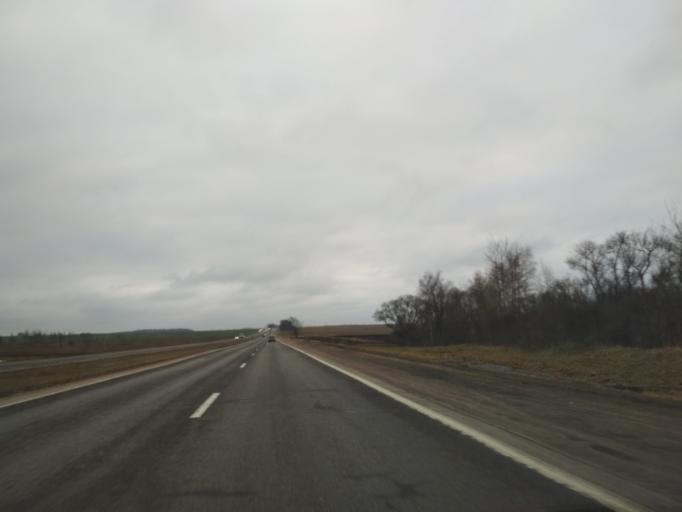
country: BY
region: Minsk
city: Blon'
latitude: 53.5607
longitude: 28.1481
